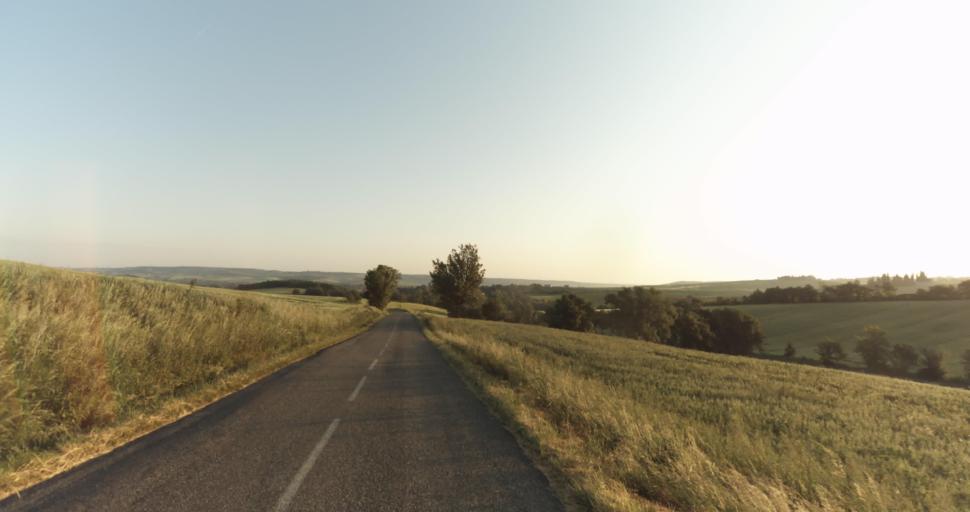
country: FR
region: Midi-Pyrenees
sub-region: Departement du Gers
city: Pujaudran
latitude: 43.6177
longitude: 1.1568
